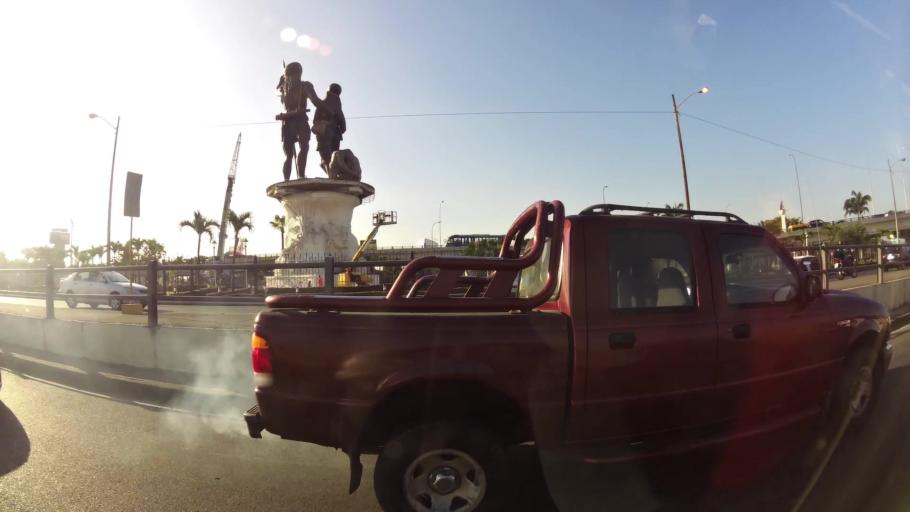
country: EC
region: Guayas
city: Eloy Alfaro
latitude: -2.1547
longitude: -79.8797
